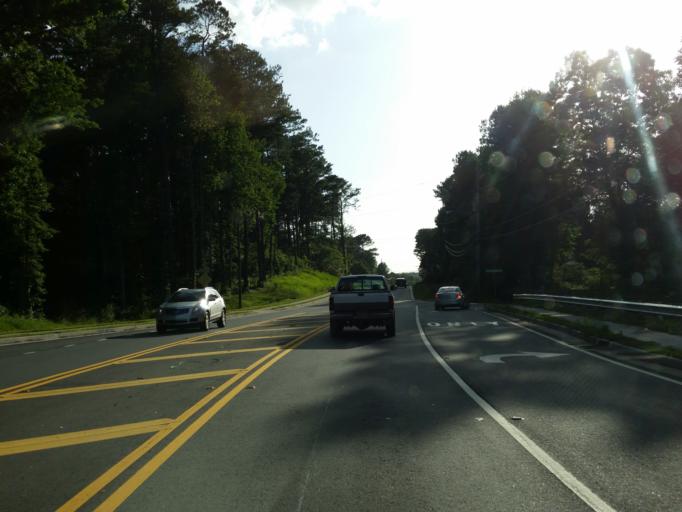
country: US
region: Georgia
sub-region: Cherokee County
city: Woodstock
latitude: 34.0682
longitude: -84.5276
